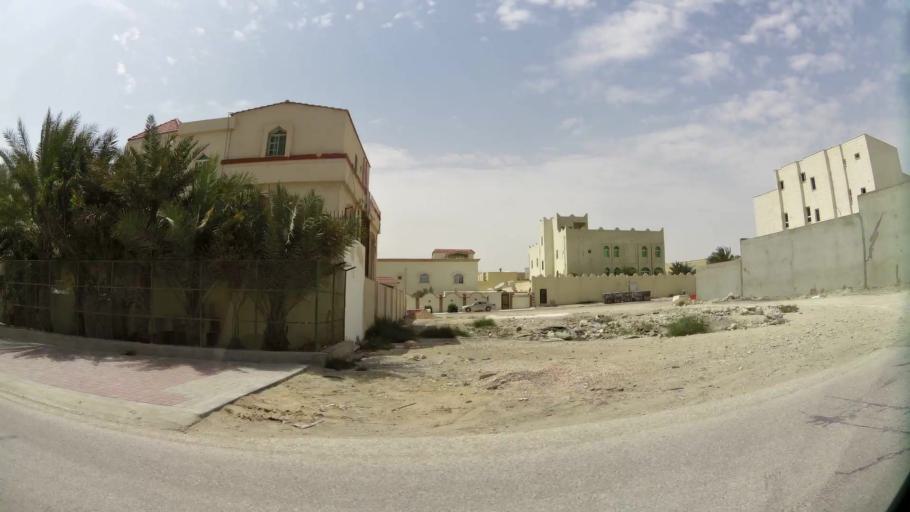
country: QA
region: Baladiyat ar Rayyan
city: Ar Rayyan
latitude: 25.3566
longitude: 51.4763
